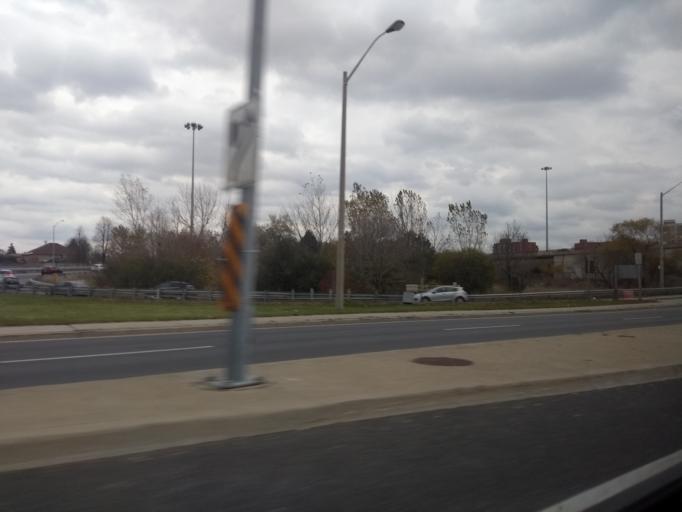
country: CA
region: Ontario
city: Etobicoke
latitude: 43.7128
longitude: -79.5065
